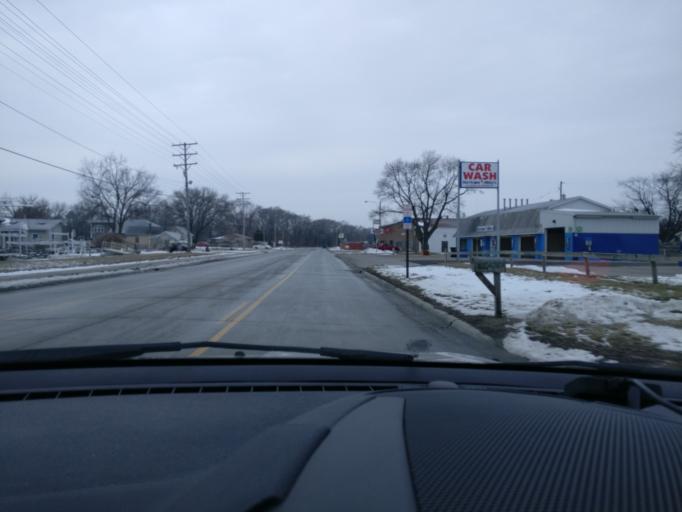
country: US
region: Nebraska
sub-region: Dodge County
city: Fremont
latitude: 41.4369
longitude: -96.5158
